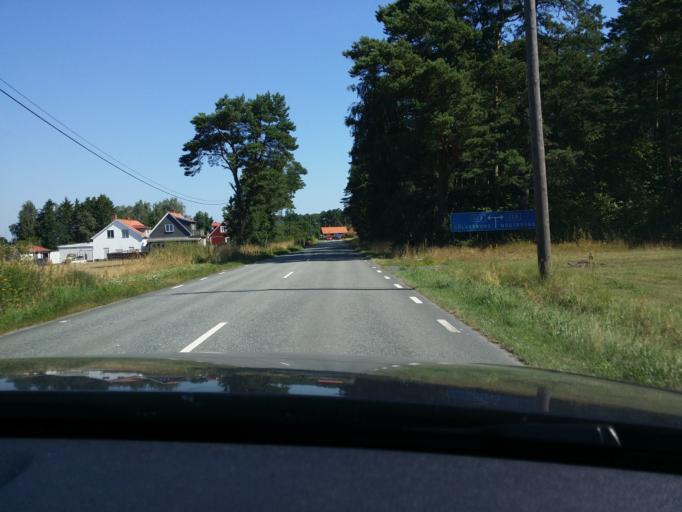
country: SE
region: Blekinge
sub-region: Solvesborgs Kommun
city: Soelvesborg
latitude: 56.0299
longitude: 14.6849
